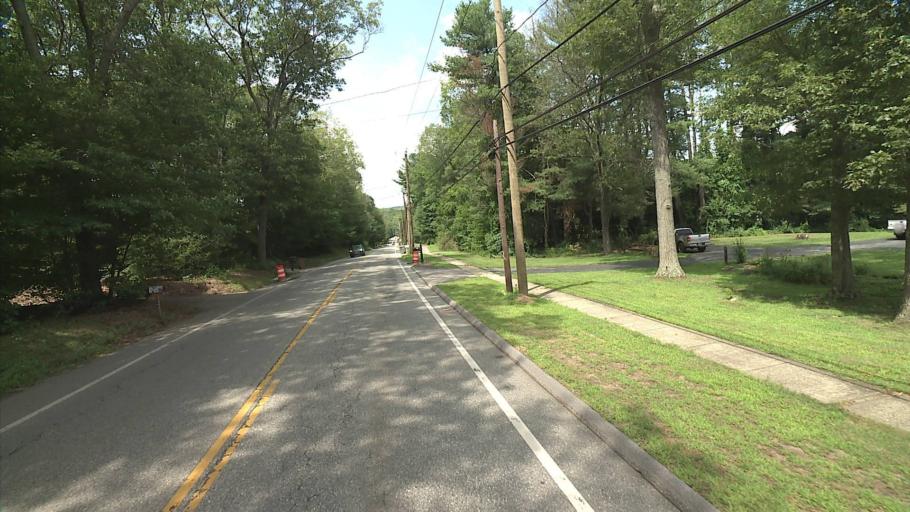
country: US
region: Connecticut
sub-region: New London County
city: Niantic
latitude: 41.3850
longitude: -72.2206
